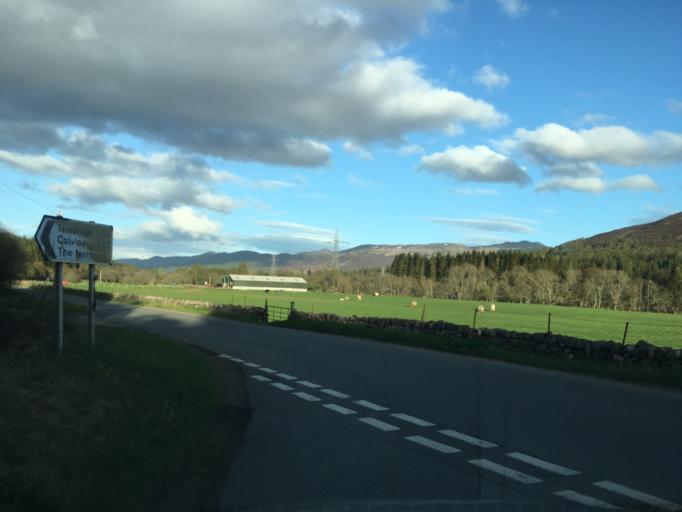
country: GB
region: Scotland
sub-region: Perth and Kinross
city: Aberfeldy
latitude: 56.7108
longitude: -4.0390
